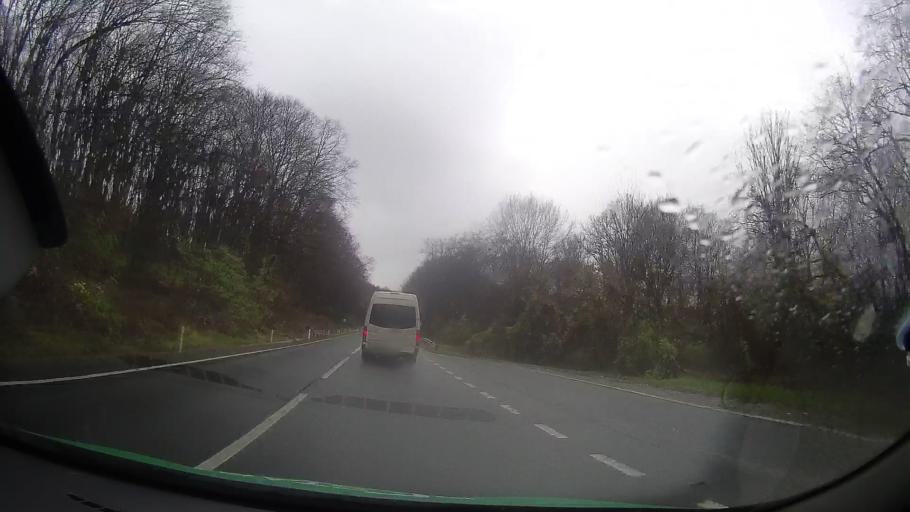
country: RO
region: Bistrita-Nasaud
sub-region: Comuna Galatii Bistritei
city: Galatii Bistritei
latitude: 47.0378
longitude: 24.4210
